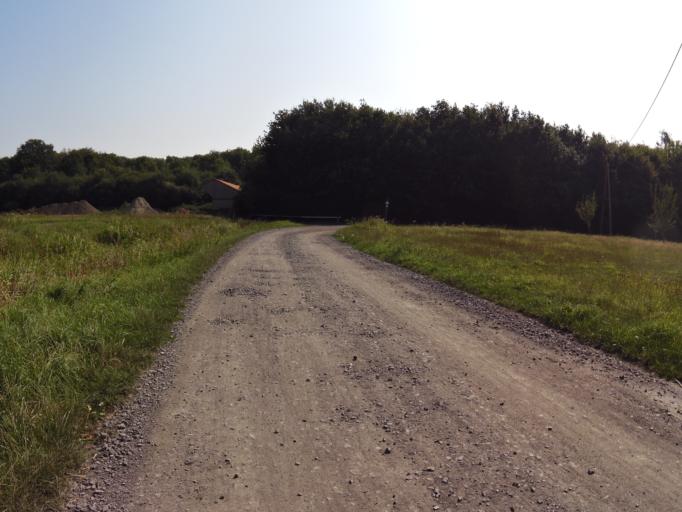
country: DE
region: North Rhine-Westphalia
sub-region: Regierungsbezirk Munster
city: Altenberge
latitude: 51.9731
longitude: 7.5007
